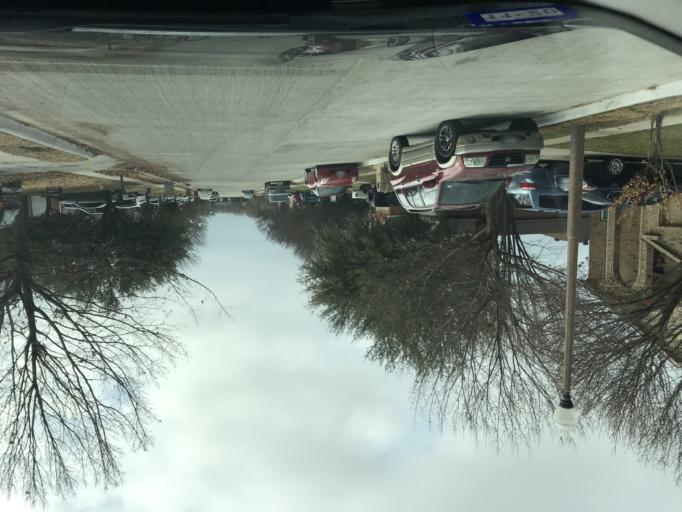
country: US
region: Texas
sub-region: Denton County
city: Denton
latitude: 33.1695
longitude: -97.1442
